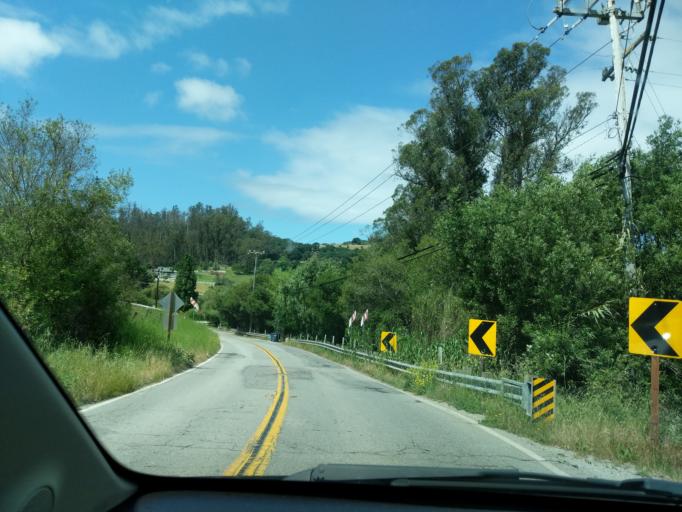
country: US
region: California
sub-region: Santa Cruz County
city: Freedom
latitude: 36.9391
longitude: -121.8056
